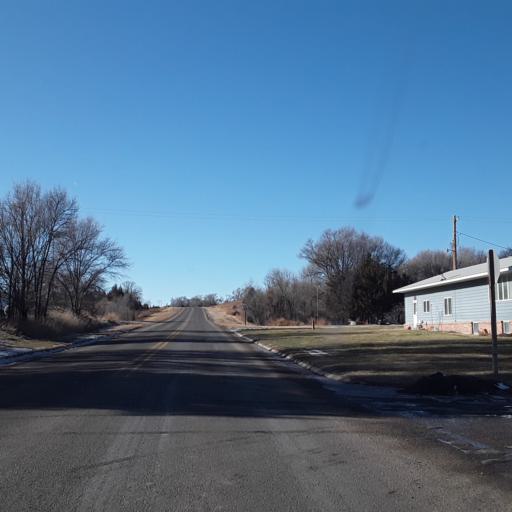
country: US
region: Nebraska
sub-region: Frontier County
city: Stockville
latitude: 40.6576
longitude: -100.6246
